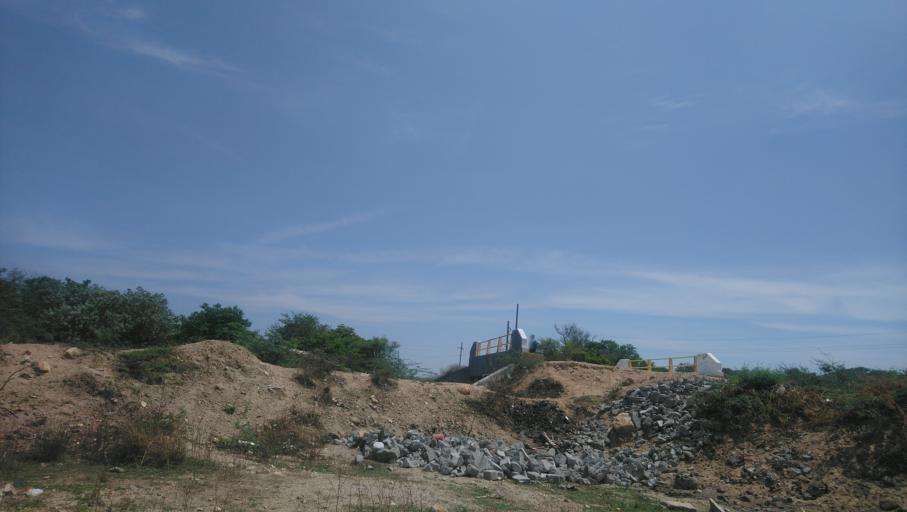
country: MX
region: Oaxaca
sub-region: Salina Cruz
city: Salina Cruz
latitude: 16.1917
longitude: -95.1190
